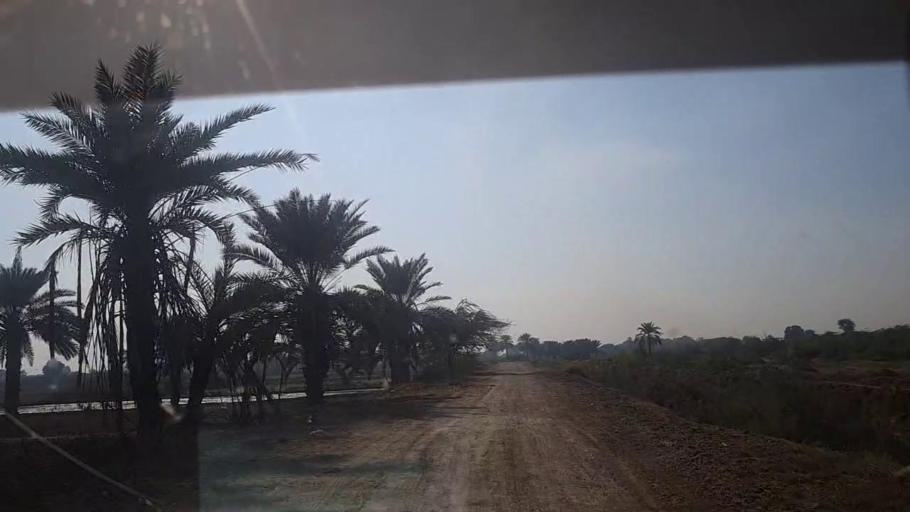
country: PK
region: Sindh
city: Gambat
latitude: 27.3770
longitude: 68.5762
